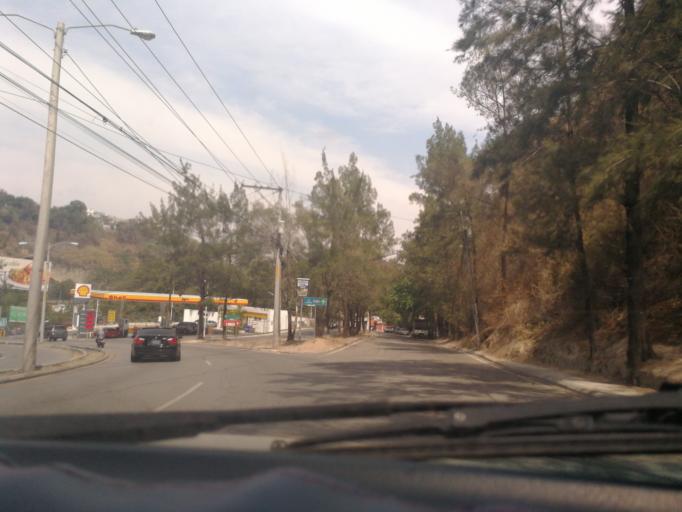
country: GT
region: Guatemala
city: Guatemala City
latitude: 14.6290
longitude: -90.4832
